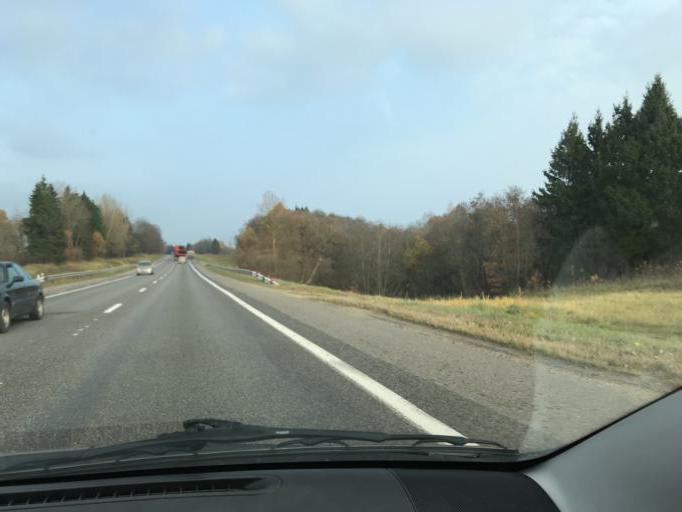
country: BY
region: Vitebsk
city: Syanno
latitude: 55.1366
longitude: 29.8155
